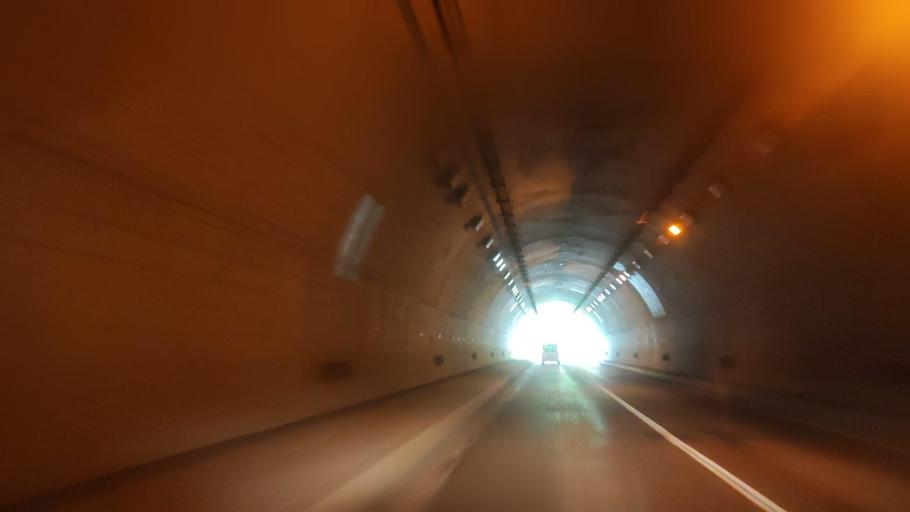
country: JP
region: Hokkaido
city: Bibai
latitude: 43.2408
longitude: 142.0275
